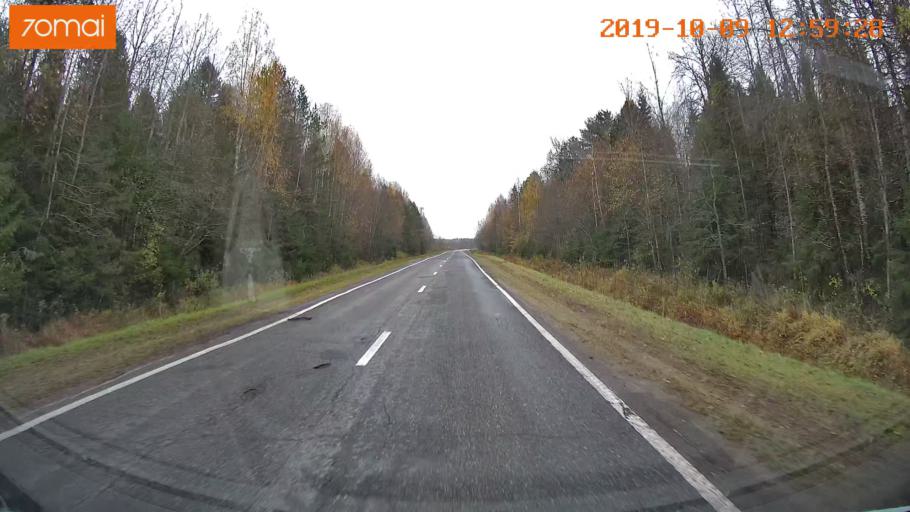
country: RU
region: Jaroslavl
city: Prechistoye
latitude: 58.3833
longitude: 40.4650
